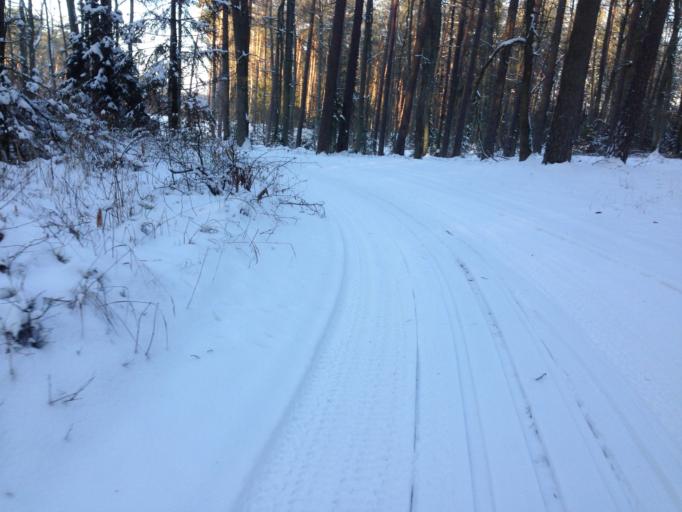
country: PL
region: Kujawsko-Pomorskie
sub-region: Powiat brodnicki
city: Gorzno
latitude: 53.1919
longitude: 19.6798
